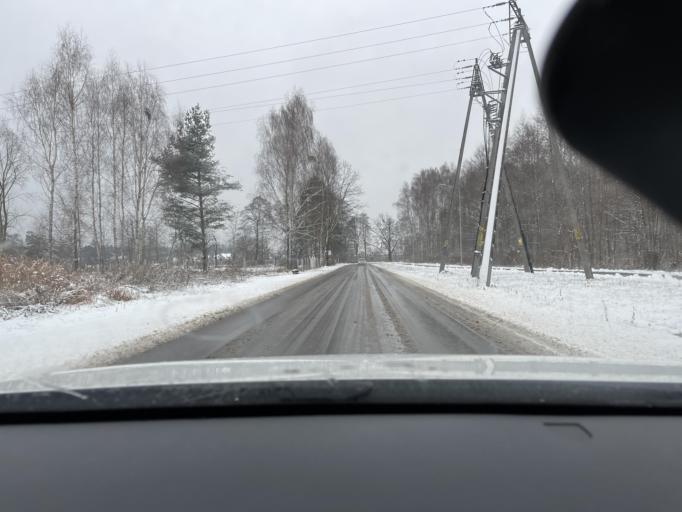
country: PL
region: Masovian Voivodeship
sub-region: Powiat zyrardowski
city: Zyrardow
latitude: 52.0374
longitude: 20.4499
